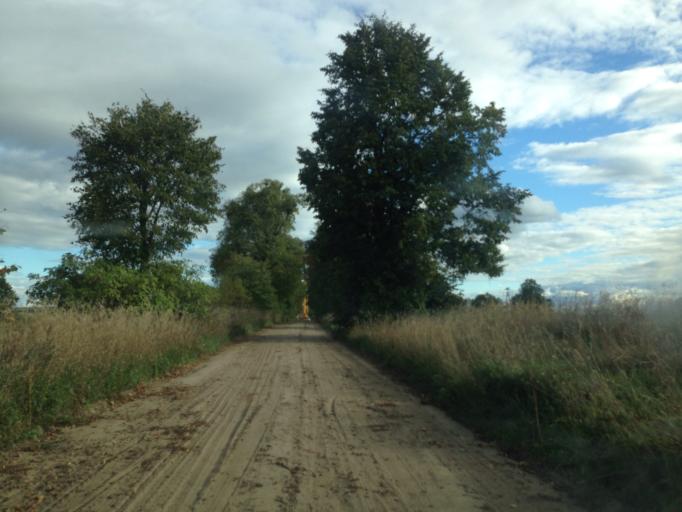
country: PL
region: Warmian-Masurian Voivodeship
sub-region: Powiat ilawski
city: Susz
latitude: 53.7448
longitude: 19.3133
